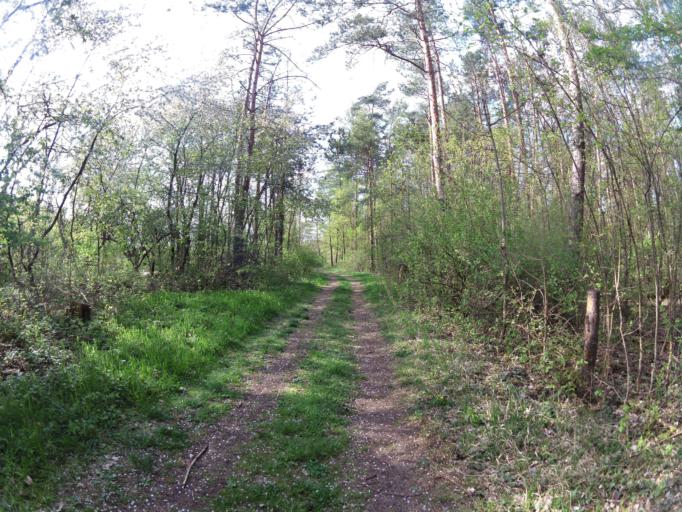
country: DE
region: Bavaria
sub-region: Regierungsbezirk Unterfranken
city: Winterhausen
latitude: 49.6974
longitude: 10.0099
